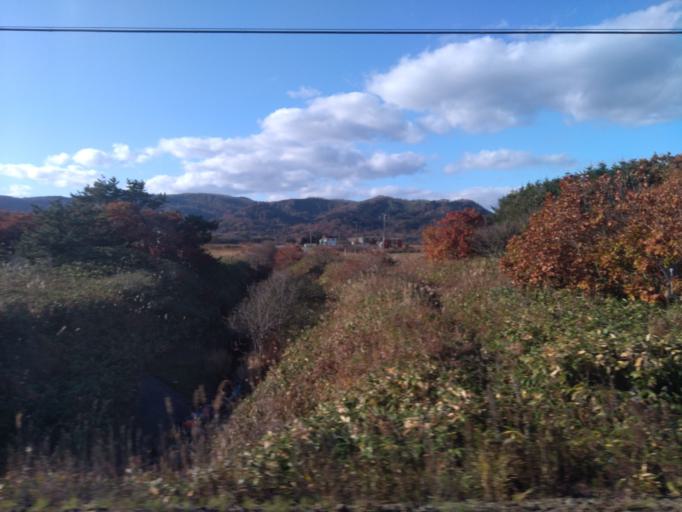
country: JP
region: Hokkaido
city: Niseko Town
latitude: 42.5722
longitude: 140.4441
